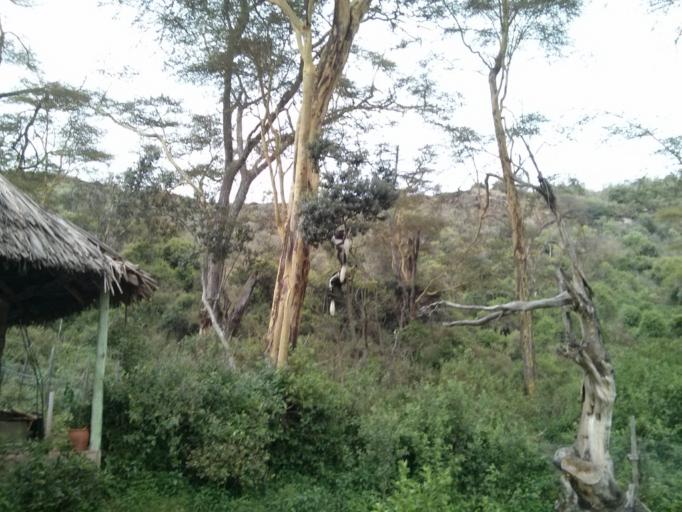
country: KE
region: Nakuru
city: Naivasha
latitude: -0.7827
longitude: 36.2599
